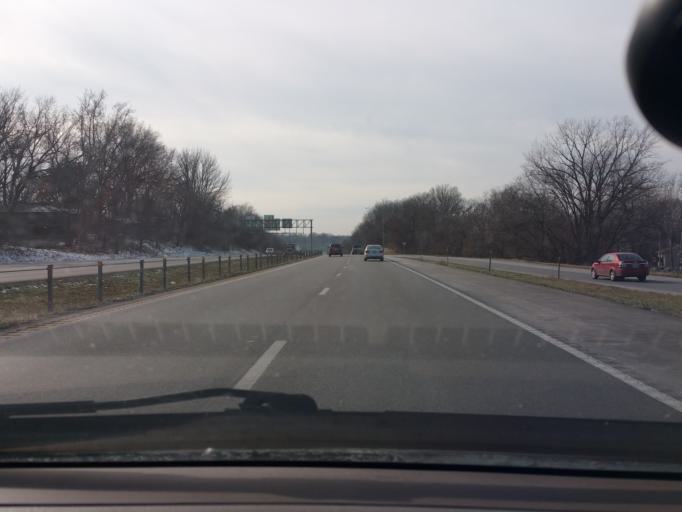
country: US
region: Missouri
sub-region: Clay County
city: Gladstone
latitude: 39.1817
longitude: -94.5247
